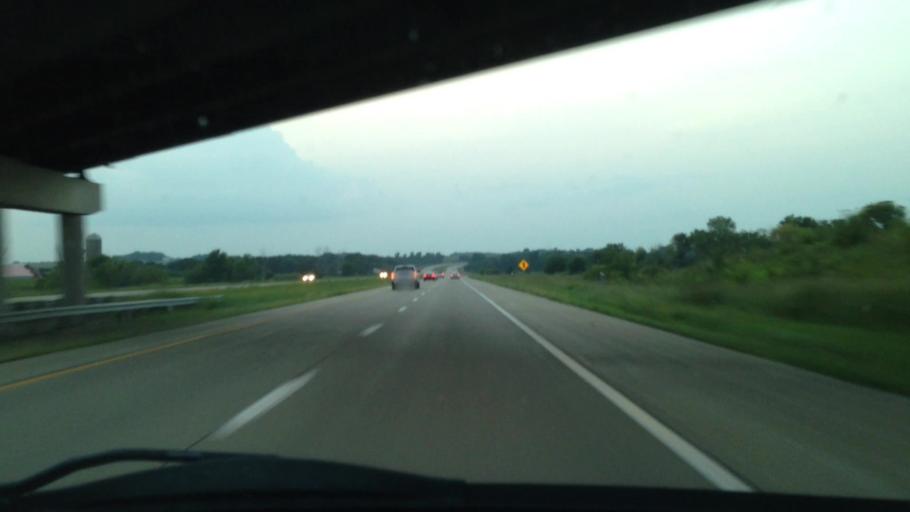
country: US
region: Iowa
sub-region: Black Hawk County
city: Elk Run Heights
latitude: 42.4134
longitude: -92.1717
